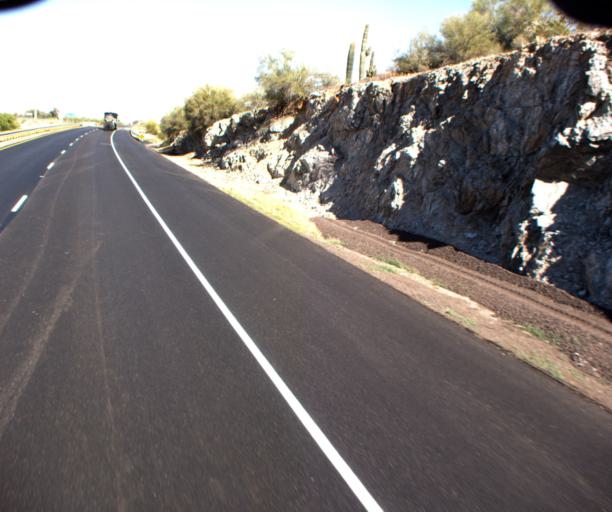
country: US
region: Arizona
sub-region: Pinal County
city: Casa Grande
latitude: 32.8345
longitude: -111.7245
